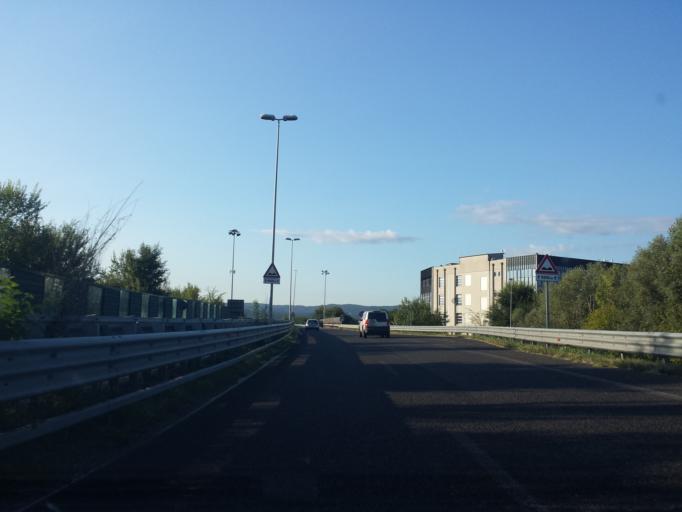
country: IT
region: Veneto
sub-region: Provincia di Vicenza
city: Creazzo
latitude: 45.5366
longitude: 11.5078
